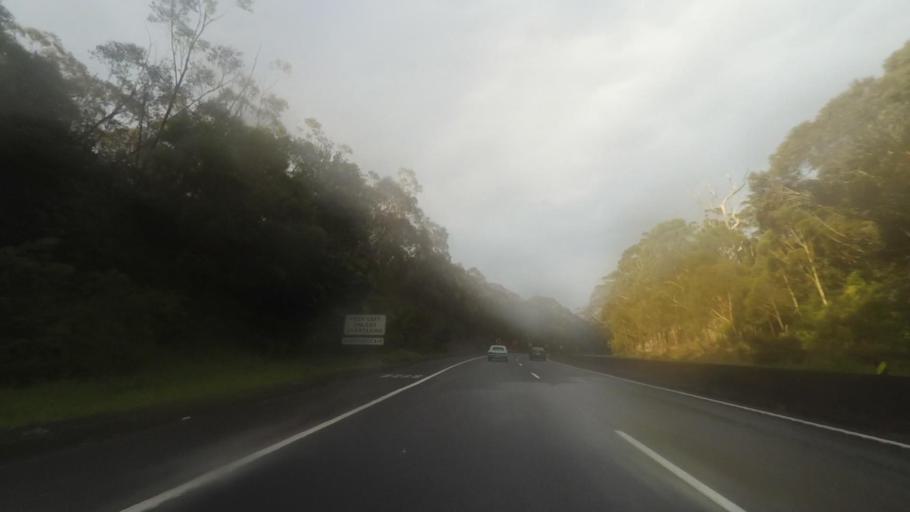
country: AU
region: New South Wales
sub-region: Wollongong
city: Bulli
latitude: -34.3465
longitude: 150.8711
